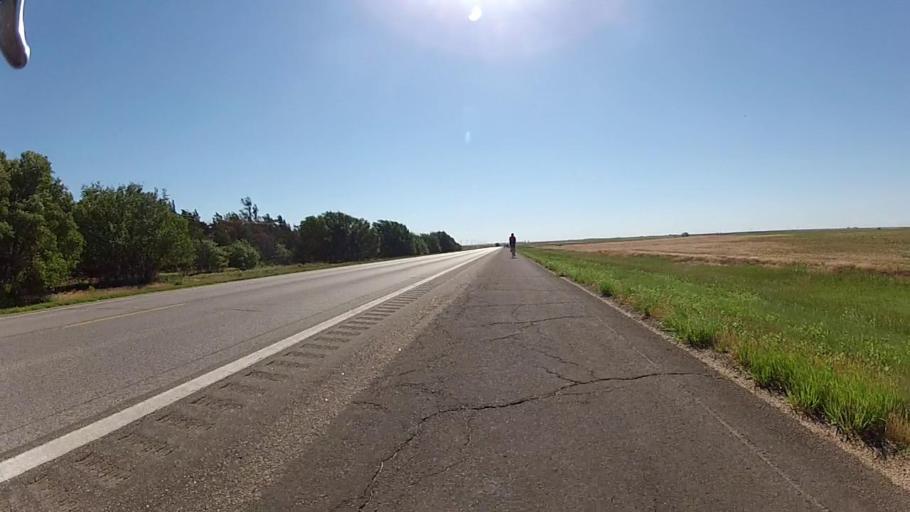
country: US
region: Kansas
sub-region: Kiowa County
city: Greensburg
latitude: 37.5864
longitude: -99.5701
